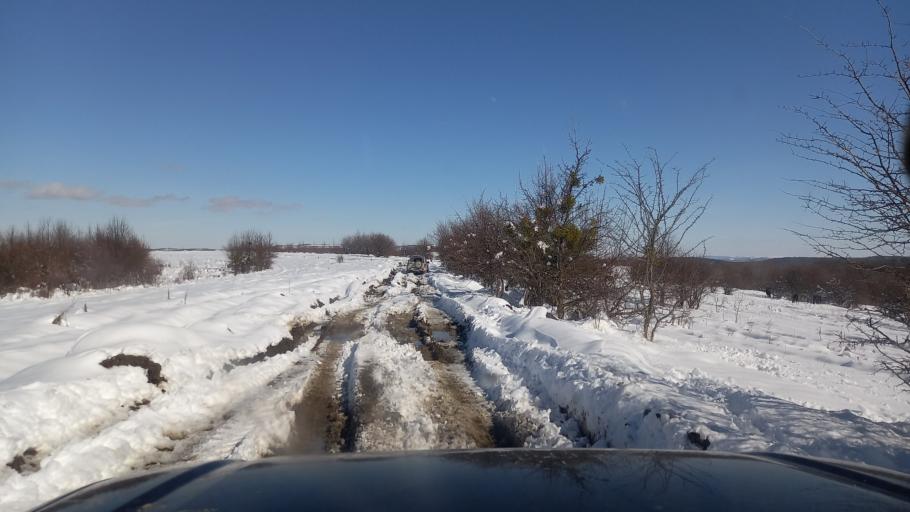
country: RU
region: Krasnodarskiy
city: Gubskaya
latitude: 44.3388
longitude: 40.4345
